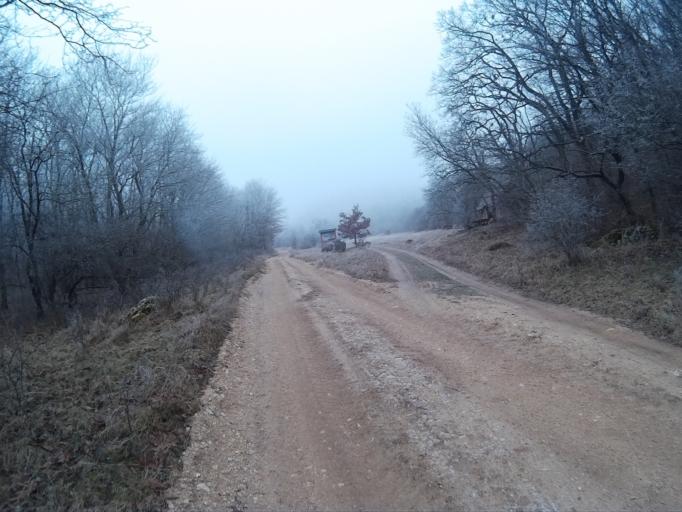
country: HU
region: Fejer
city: Zamoly
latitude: 47.3909
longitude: 18.3662
